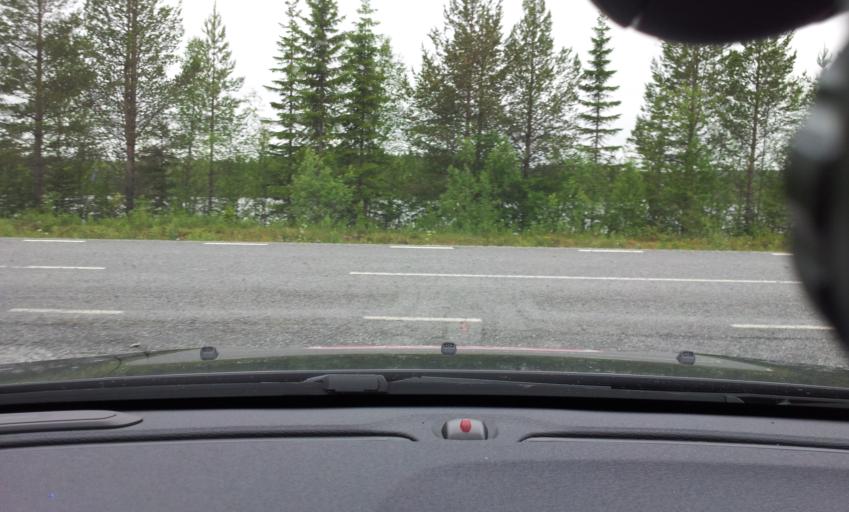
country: SE
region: Jaemtland
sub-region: OEstersunds Kommun
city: Lit
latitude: 63.6844
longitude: 14.6726
